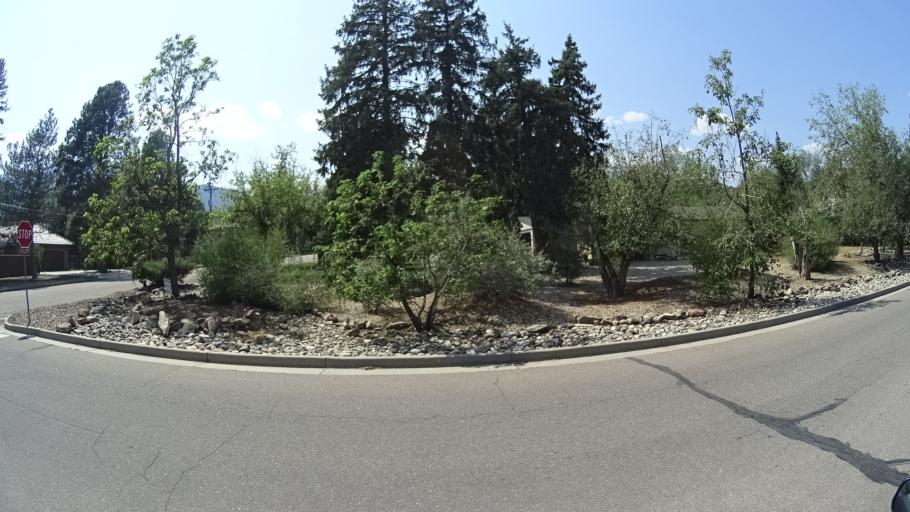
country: US
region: Colorado
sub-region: El Paso County
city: Colorado Springs
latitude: 38.7938
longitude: -104.8442
